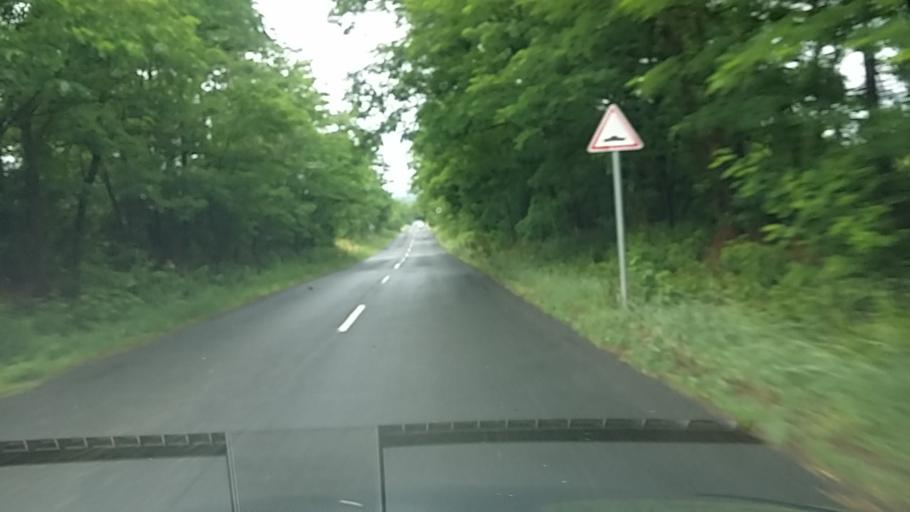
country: SK
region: Nitriansky
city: Sahy
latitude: 47.9892
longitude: 18.8200
